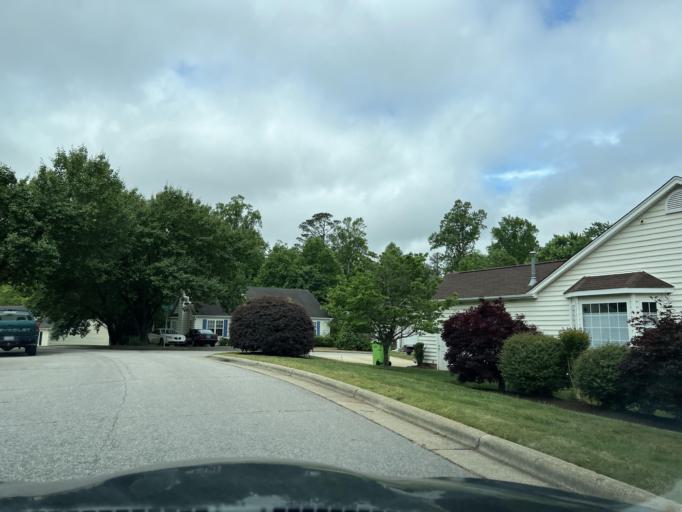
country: US
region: North Carolina
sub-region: Wake County
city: Knightdale
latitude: 35.8688
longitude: -78.5517
